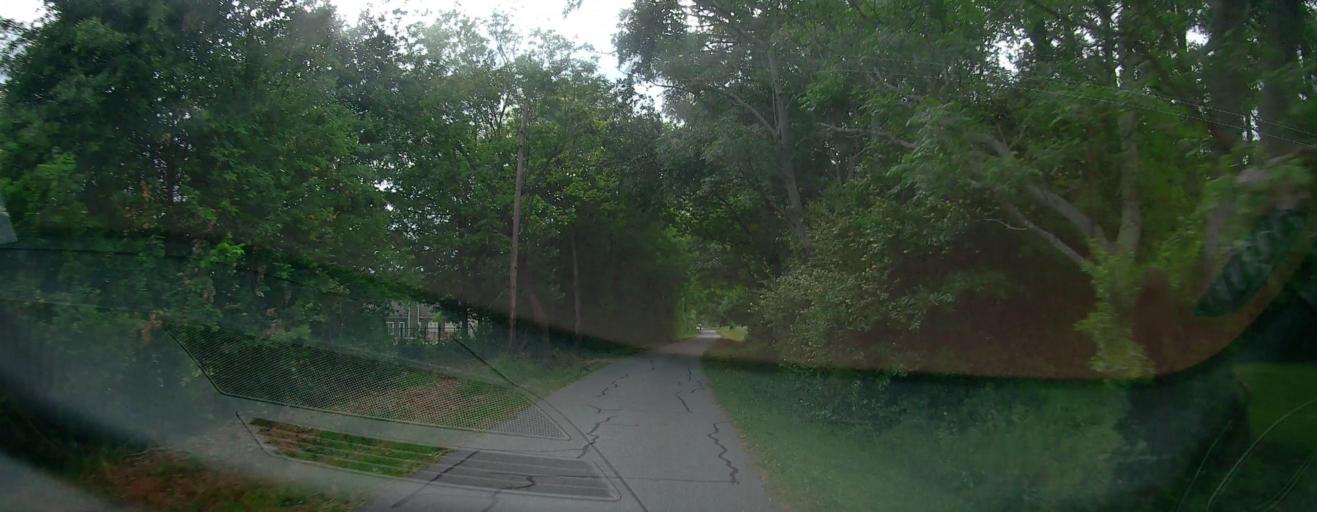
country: US
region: Georgia
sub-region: Oconee County
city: Watkinsville
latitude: 33.8210
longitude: -83.4415
